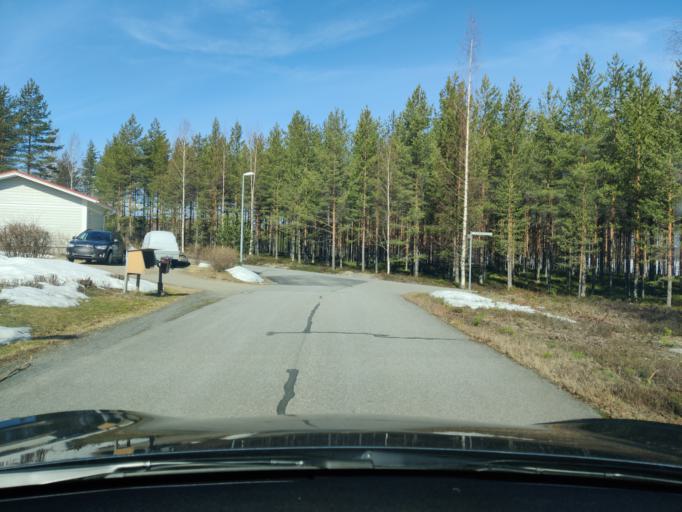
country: FI
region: Northern Savo
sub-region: Kuopio
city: Vehmersalmi
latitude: 62.7730
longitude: 27.9849
